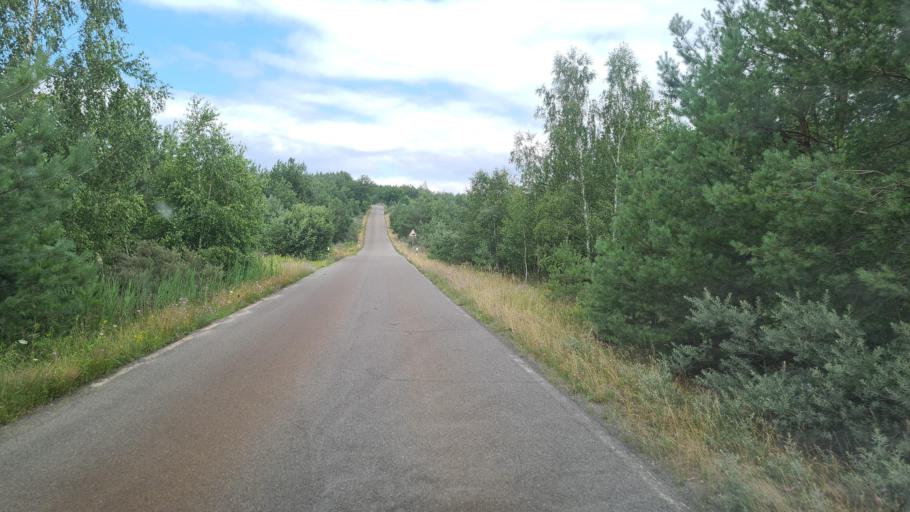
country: DE
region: Brandenburg
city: Neupetershain
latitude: 51.6466
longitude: 14.1083
